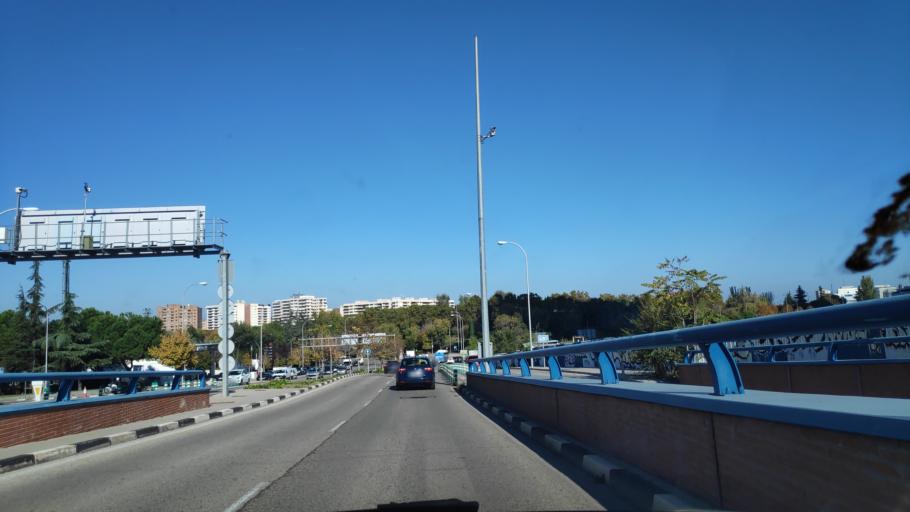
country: ES
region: Madrid
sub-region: Provincia de Madrid
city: Chamartin
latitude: 40.4767
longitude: -3.6903
